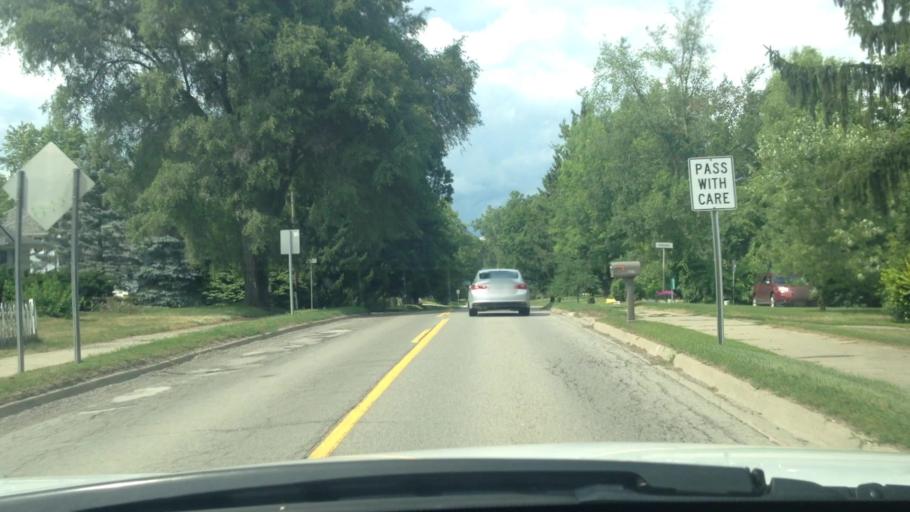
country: US
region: Michigan
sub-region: Oakland County
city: Clarkston
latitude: 42.7665
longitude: -83.3416
